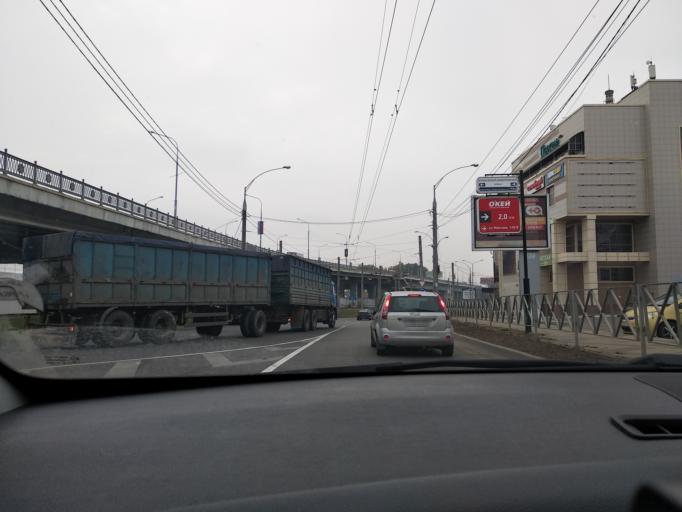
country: RU
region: Krasnodarskiy
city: Krasnodar
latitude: 45.0380
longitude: 38.9546
